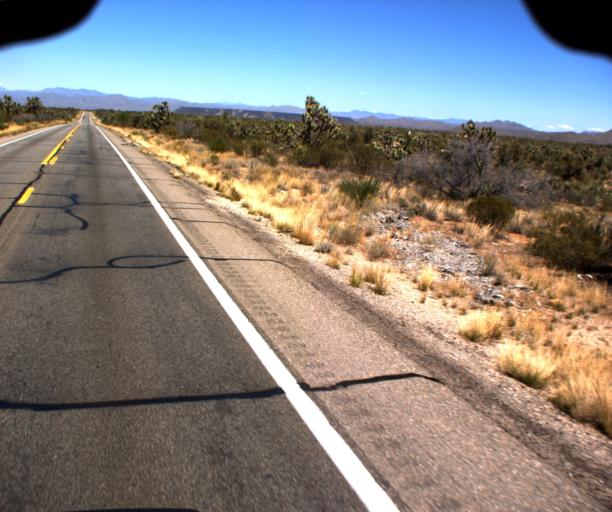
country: US
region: Arizona
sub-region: Yavapai County
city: Congress
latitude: 34.2560
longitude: -113.0853
